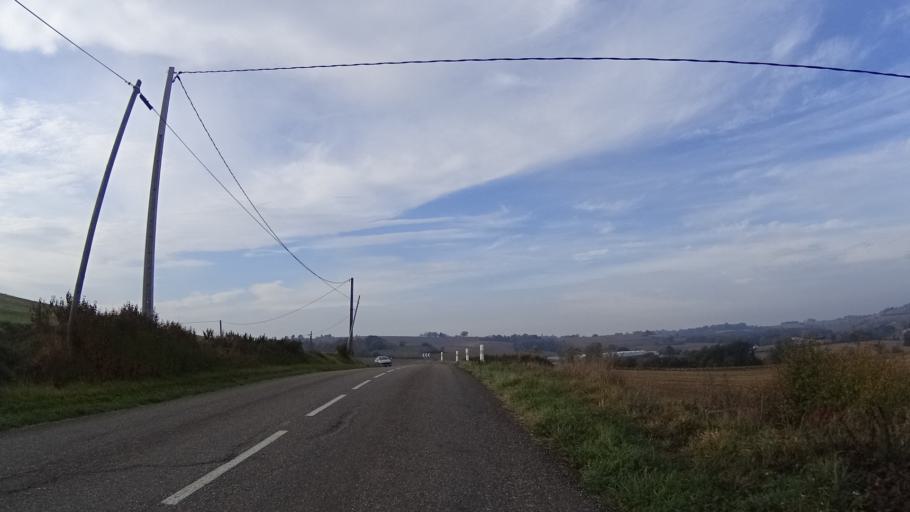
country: FR
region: Aquitaine
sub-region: Departement du Lot-et-Garonne
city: Laplume
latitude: 44.1026
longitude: 0.5660
